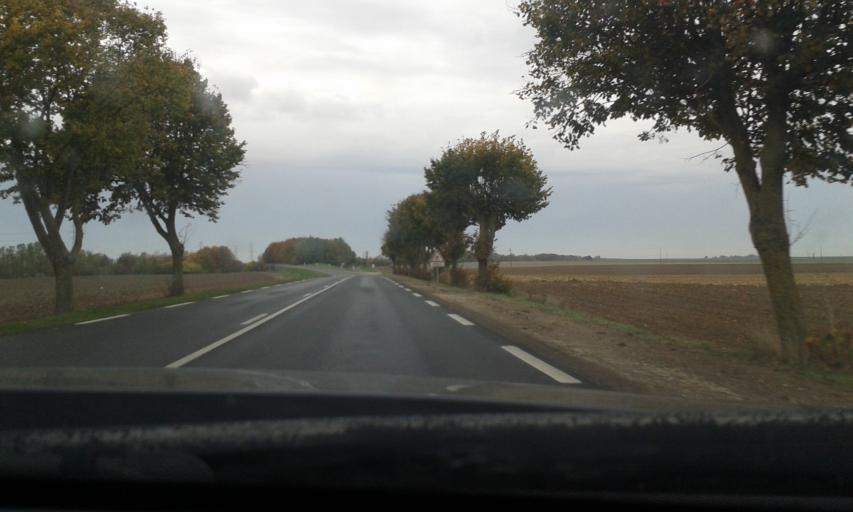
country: FR
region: Centre
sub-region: Departement d'Eure-et-Loir
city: Baigneaux
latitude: 48.1248
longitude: 1.8561
